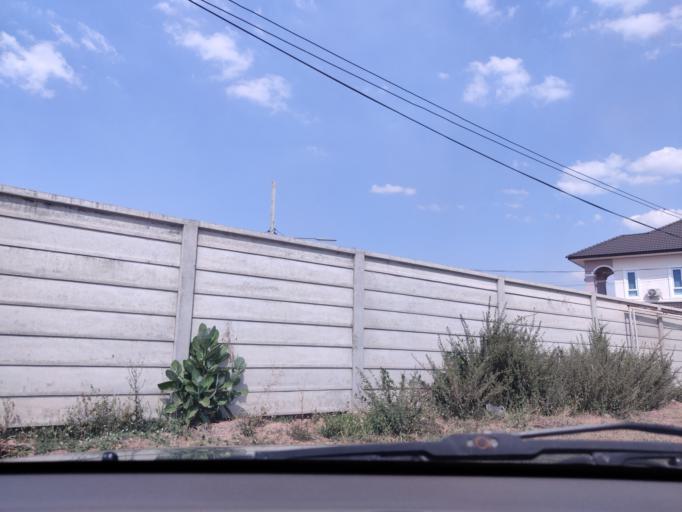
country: TH
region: Sisaket
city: Si Sa Ket
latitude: 15.0999
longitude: 104.3568
